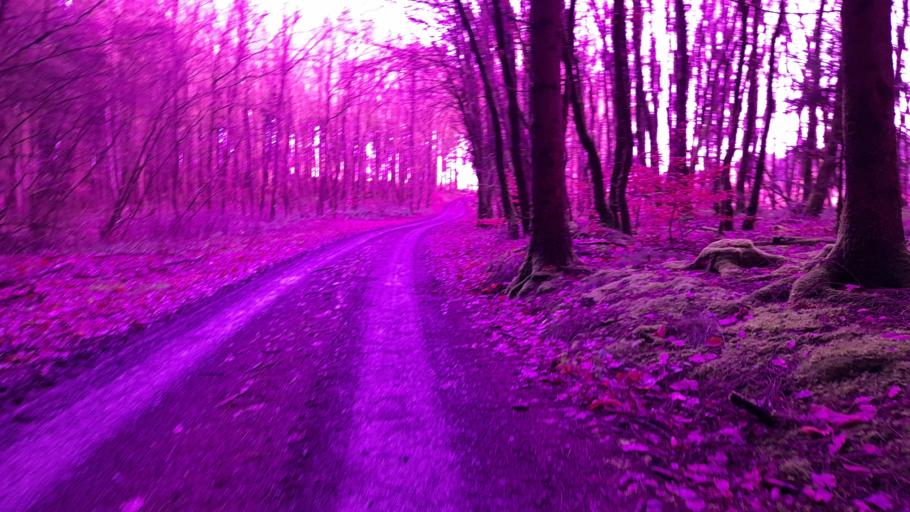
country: DE
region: Rheinland-Pfalz
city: Dasburg
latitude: 50.0842
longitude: 6.1052
